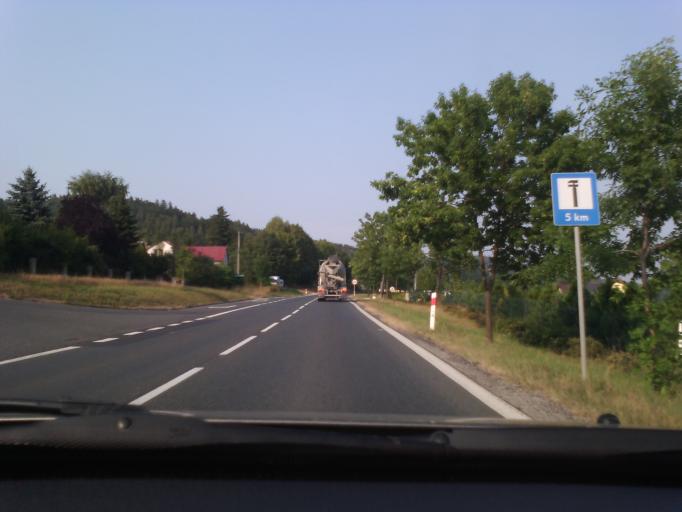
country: PL
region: Lower Silesian Voivodeship
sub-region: Powiat jeleniogorski
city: Piechowice
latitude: 50.8806
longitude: 15.6336
